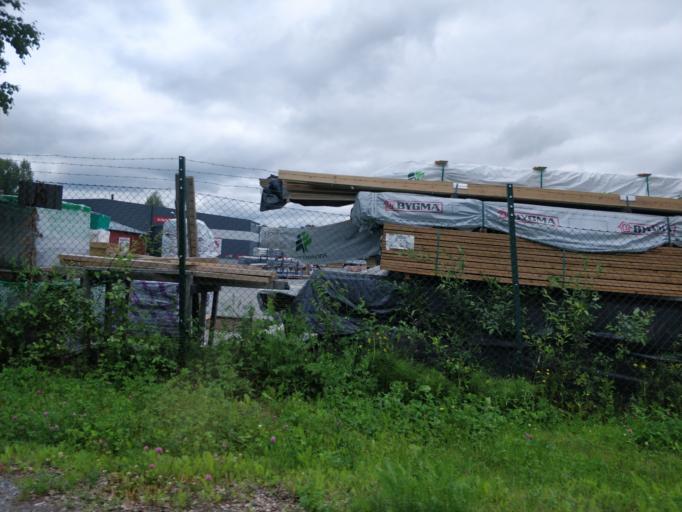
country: SE
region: Vaesterbotten
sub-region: Skelleftea Kommun
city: Viken
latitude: 64.7598
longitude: 20.8892
